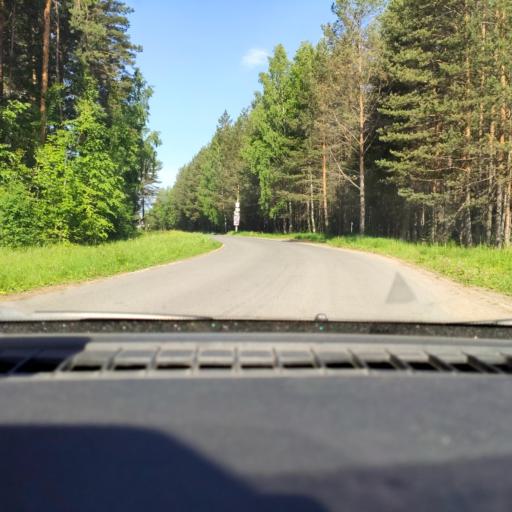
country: RU
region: Perm
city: Overyata
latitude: 57.9978
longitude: 55.8805
